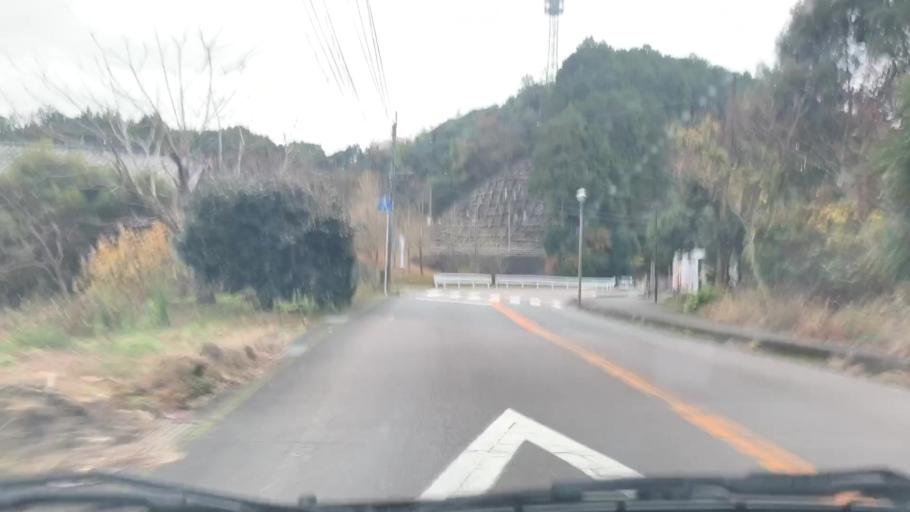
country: JP
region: Saga Prefecture
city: Ureshinomachi-shimojuku
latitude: 33.1049
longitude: 129.9782
